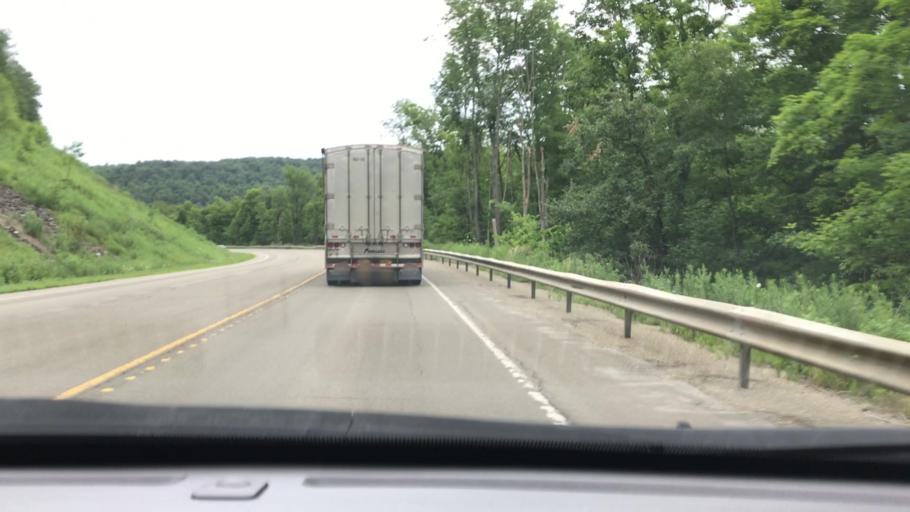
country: US
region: Pennsylvania
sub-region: McKean County
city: Kane
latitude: 41.7579
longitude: -78.6981
